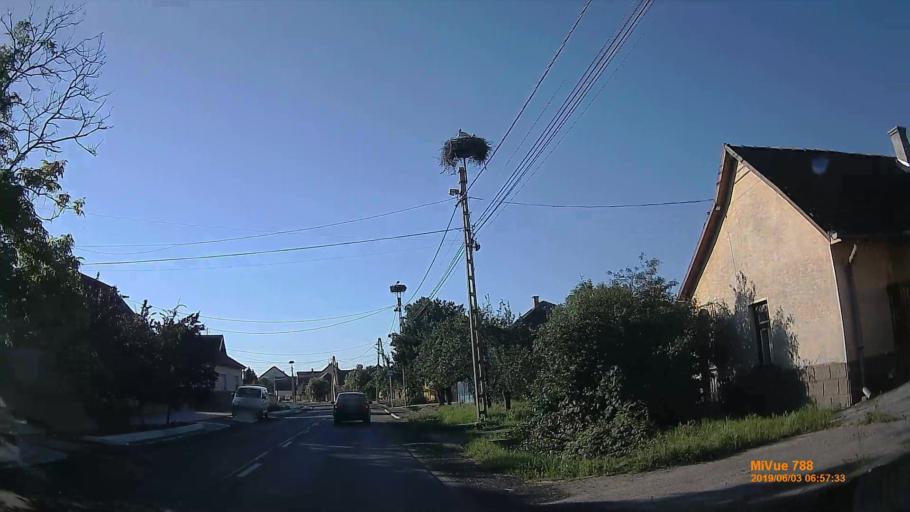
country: HU
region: Pest
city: Dabas
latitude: 47.2171
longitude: 19.2676
